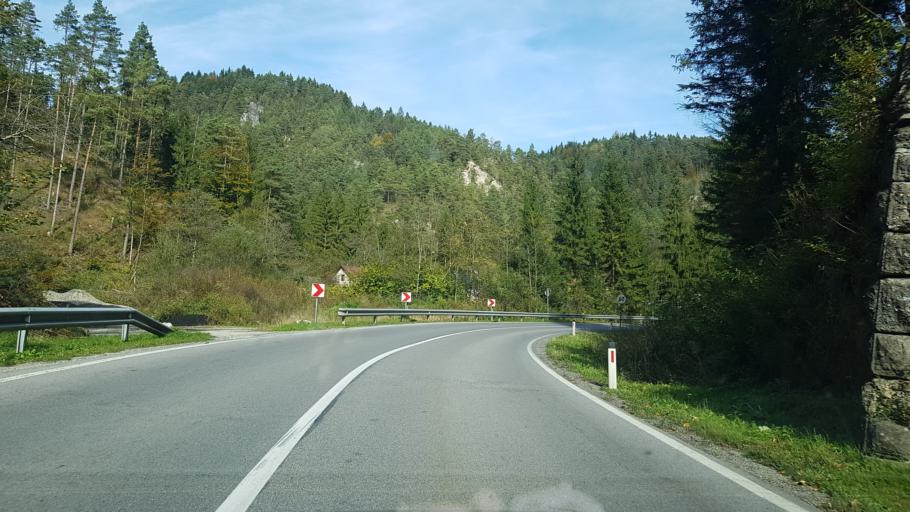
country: SI
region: Velenje
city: Velenje
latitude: 46.4193
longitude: 15.1742
